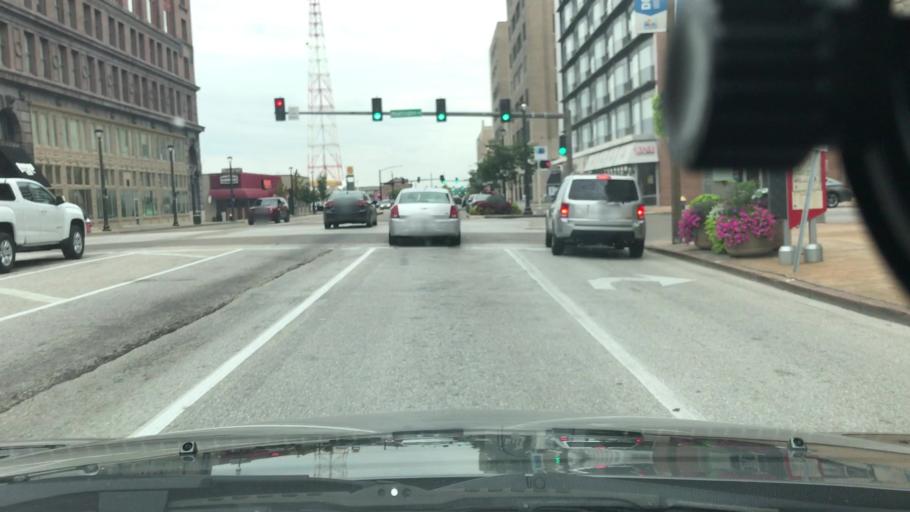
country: US
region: Missouri
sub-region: City of Saint Louis
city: St. Louis
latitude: 38.6315
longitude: -90.1967
